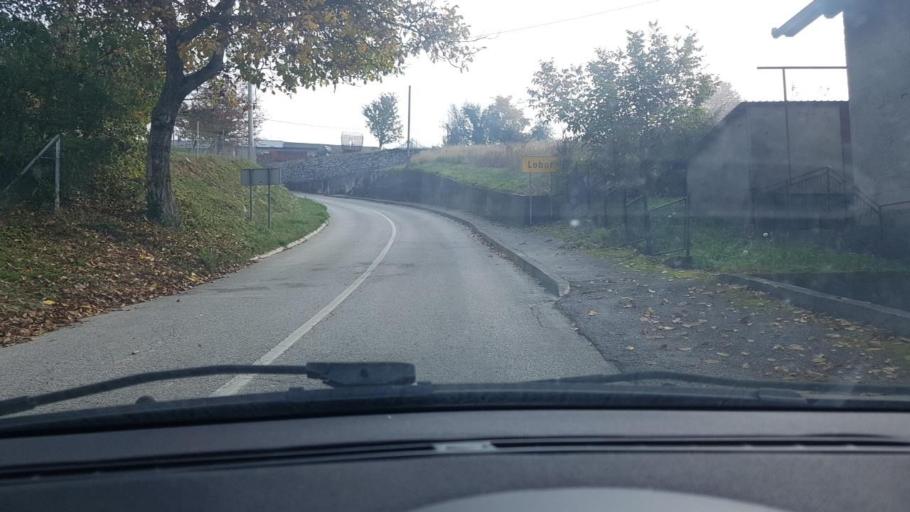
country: HR
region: Krapinsko-Zagorska
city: Zlatar
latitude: 46.1486
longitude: 16.0595
